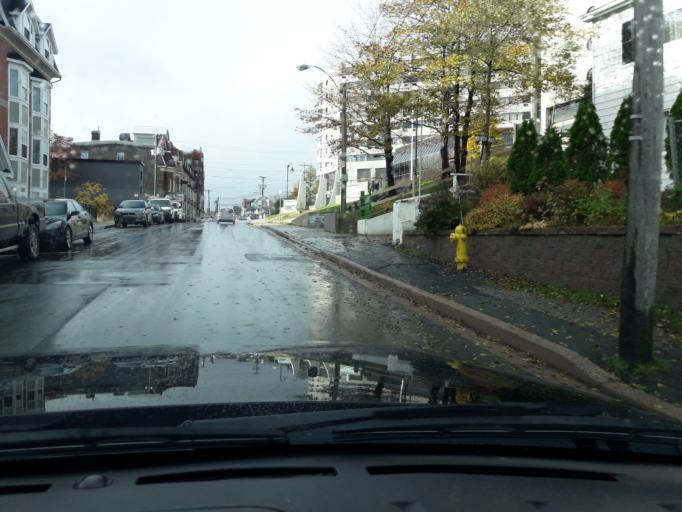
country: CA
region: Newfoundland and Labrador
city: St. John's
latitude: 47.5713
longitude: -52.6987
